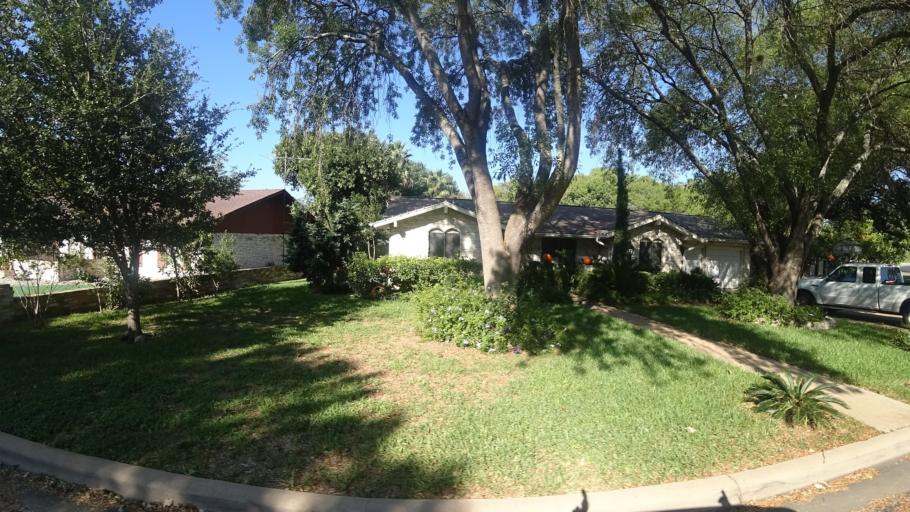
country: US
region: Texas
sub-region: Travis County
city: Austin
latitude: 30.3232
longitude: -97.6747
